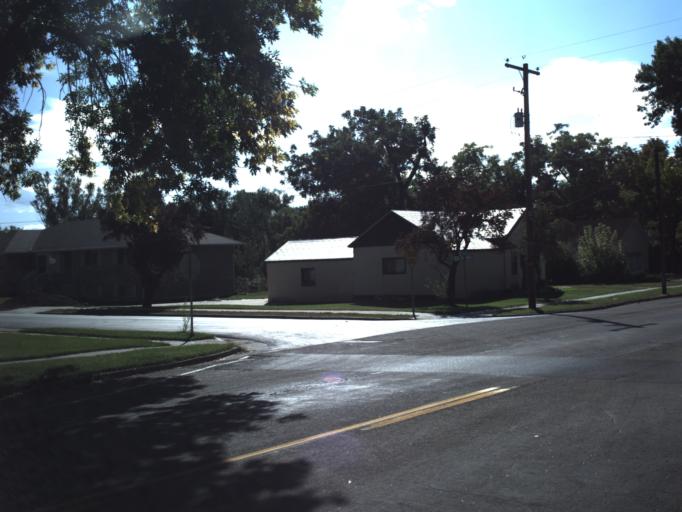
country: US
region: Utah
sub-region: Davis County
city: Farmington
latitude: 40.9805
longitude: -111.8895
